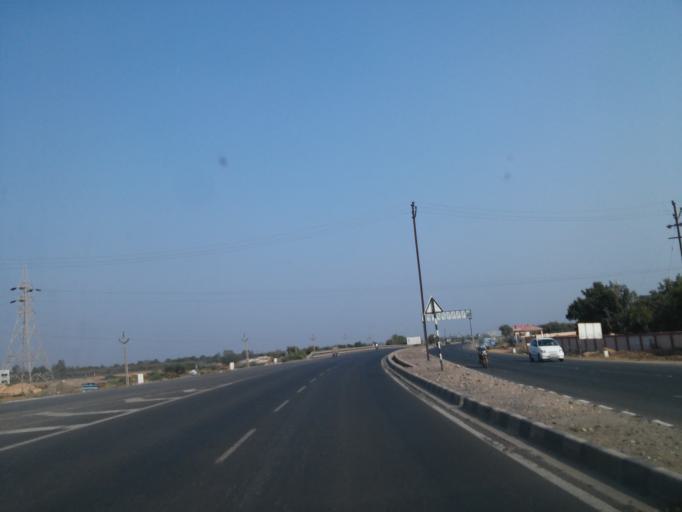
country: IN
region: Gujarat
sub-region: Surendranagar
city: Halvad
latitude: 23.0155
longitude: 71.2037
